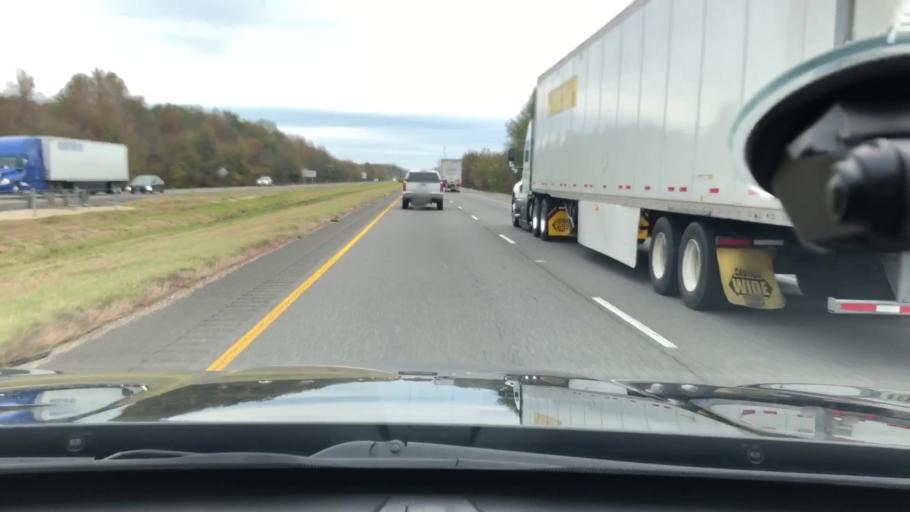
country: US
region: Arkansas
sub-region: Clark County
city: Gurdon
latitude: 34.0040
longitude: -93.1765
